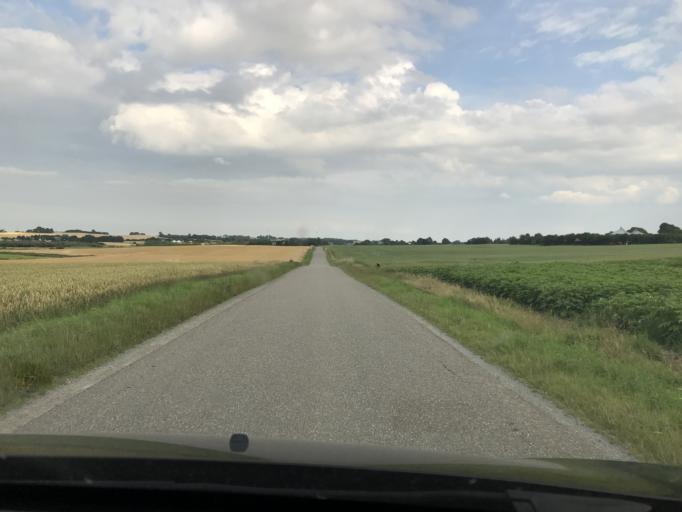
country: DK
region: South Denmark
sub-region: Vejle Kommune
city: Jelling
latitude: 55.8043
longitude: 9.4386
